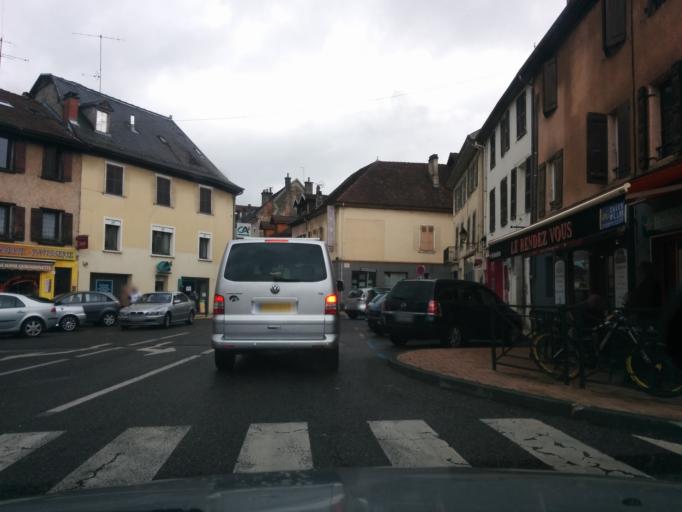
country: FR
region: Rhone-Alpes
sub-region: Departement de la Savoie
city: Le Pont-de-Beauvoisin
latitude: 45.5364
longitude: 5.6698
